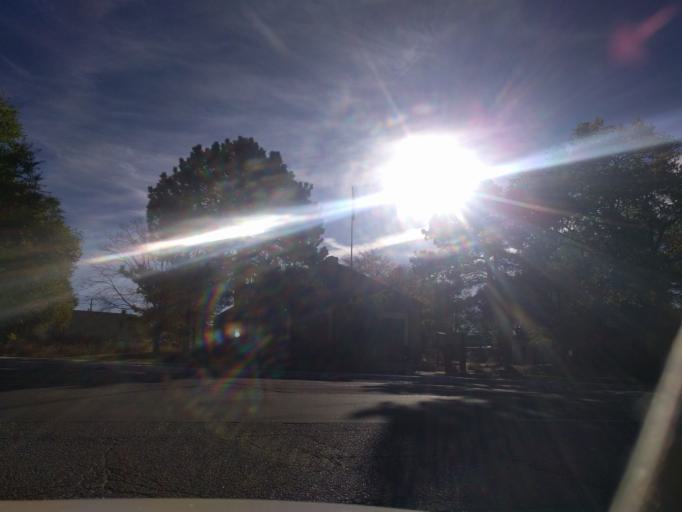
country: US
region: Colorado
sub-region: El Paso County
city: Colorado Springs
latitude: 38.8253
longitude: -104.8205
